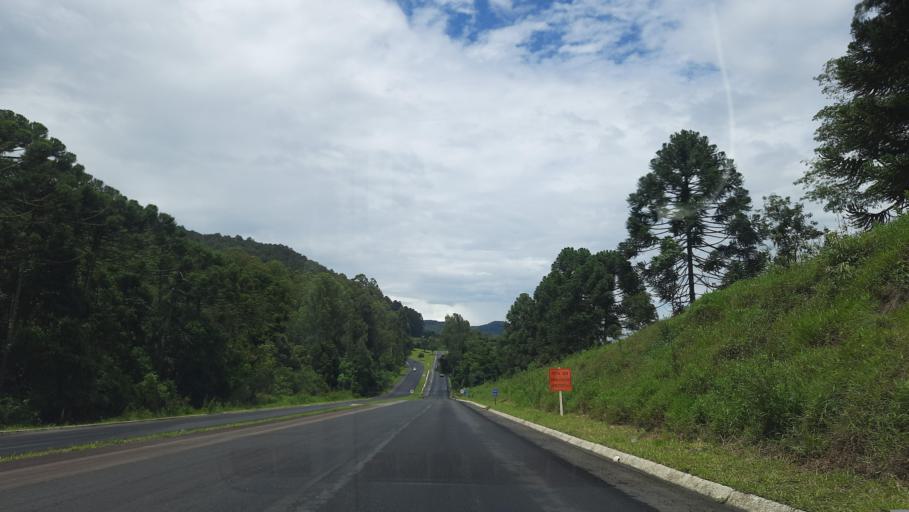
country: BR
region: Minas Gerais
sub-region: Pocos De Caldas
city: Pocos de Caldas
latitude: -21.8051
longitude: -46.6525
